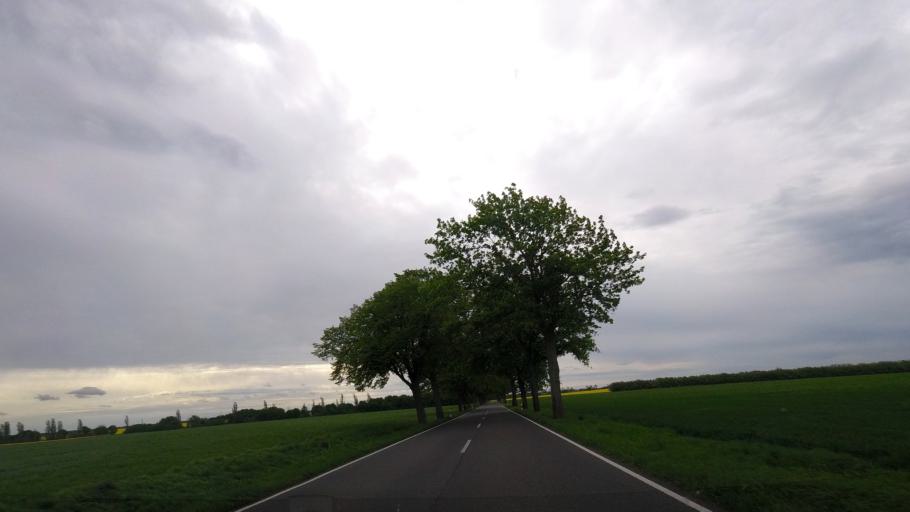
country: DE
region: Brandenburg
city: Ihlow
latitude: 51.9255
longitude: 13.2130
